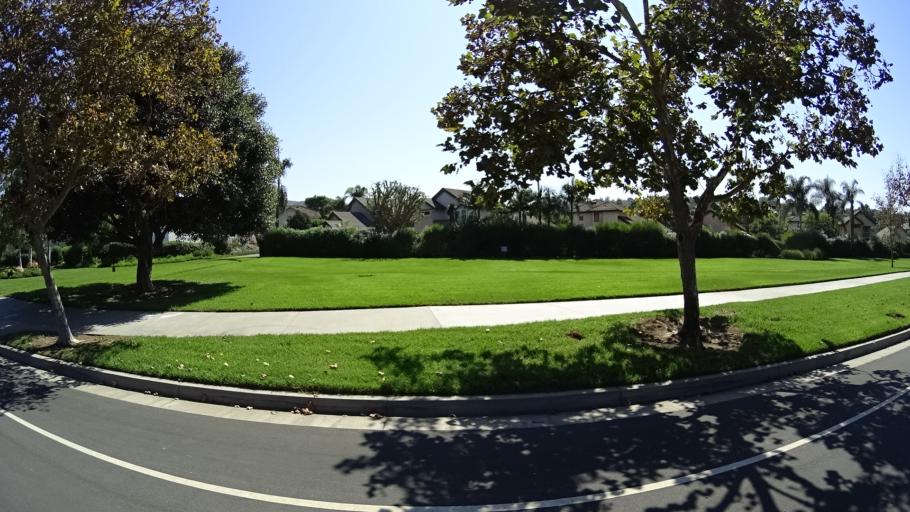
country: US
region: California
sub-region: Orange County
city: San Juan Capistrano
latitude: 33.4709
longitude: -117.6303
